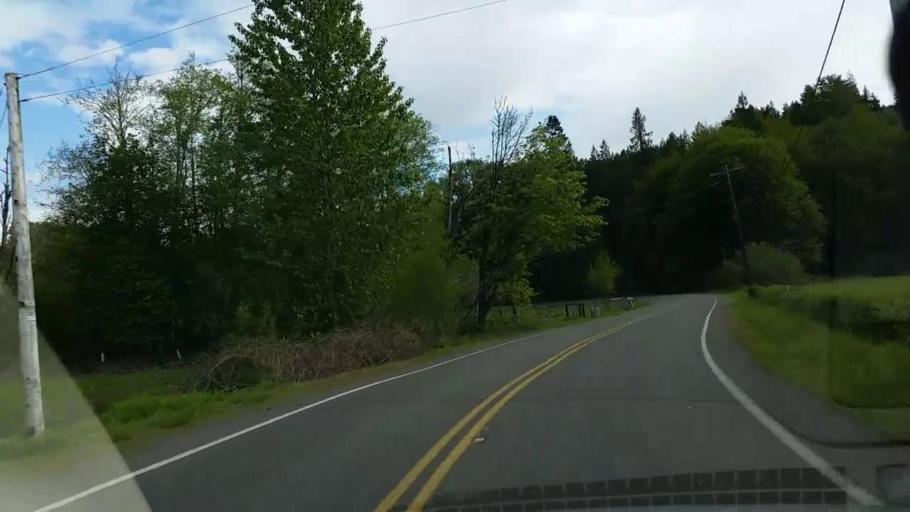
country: US
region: Washington
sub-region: Mason County
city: Shelton
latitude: 47.3174
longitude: -123.2579
